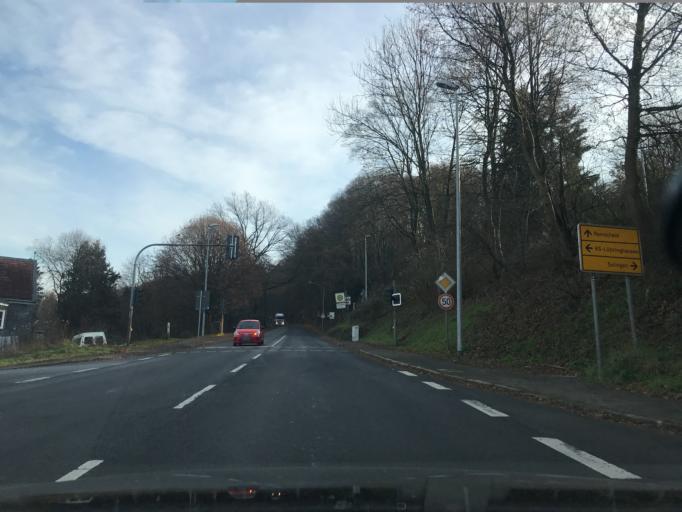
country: DE
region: North Rhine-Westphalia
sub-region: Regierungsbezirk Dusseldorf
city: Remscheid
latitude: 51.2005
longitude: 7.1598
